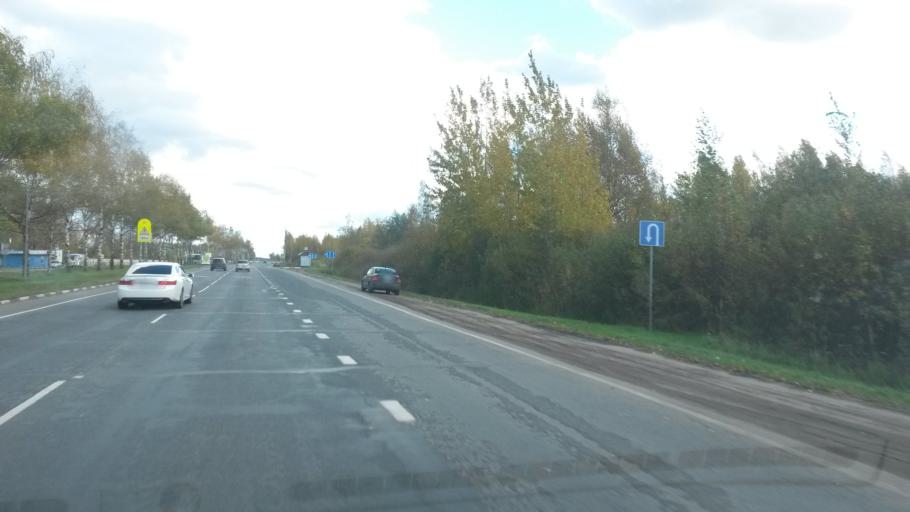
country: RU
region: Jaroslavl
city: Yaroslavl
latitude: 57.5409
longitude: 39.9759
